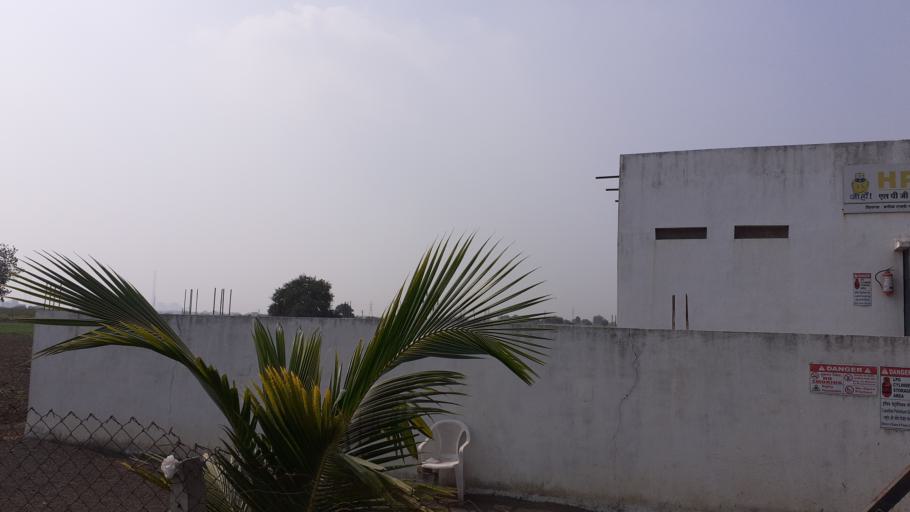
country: IN
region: Maharashtra
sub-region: Chandrapur
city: Warora
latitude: 20.3051
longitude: 79.0157
